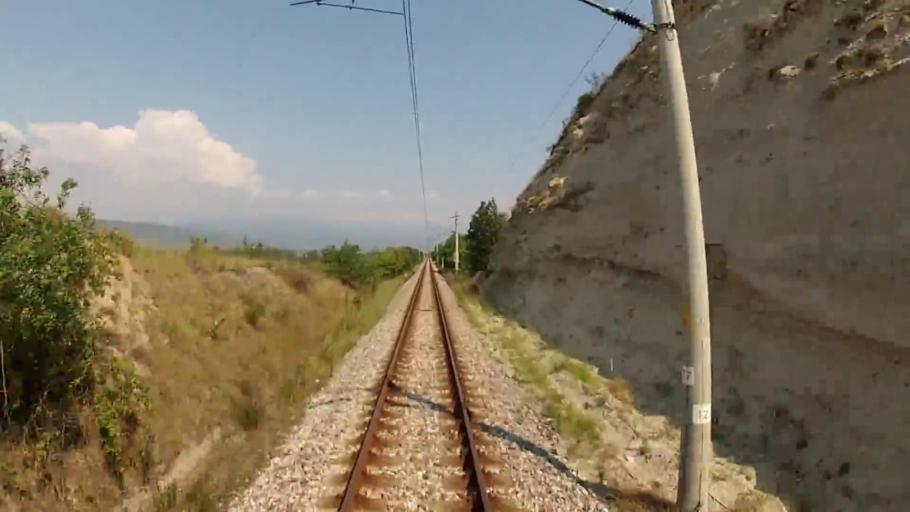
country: BG
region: Blagoevgrad
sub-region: Obshtina Strumyani
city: Strumyani
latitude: 41.6060
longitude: 23.2274
